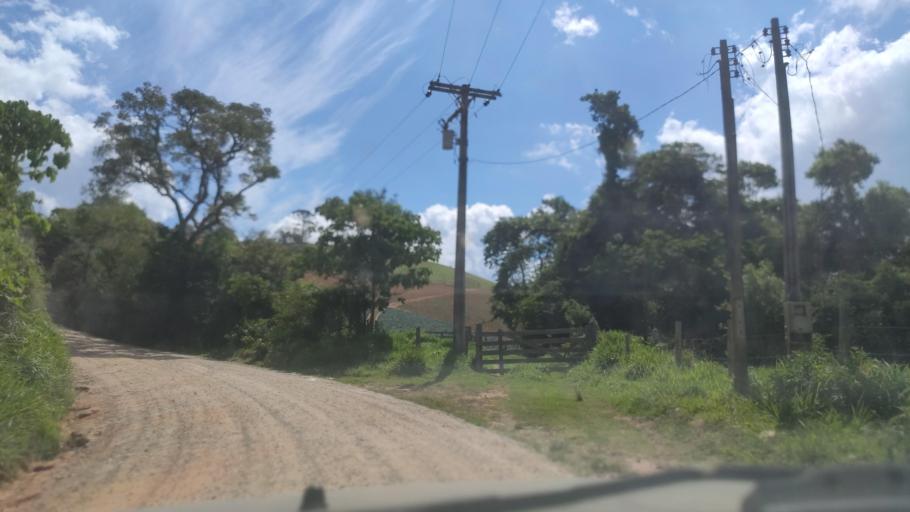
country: BR
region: Minas Gerais
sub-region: Cambui
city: Cambui
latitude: -22.7139
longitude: -46.0372
